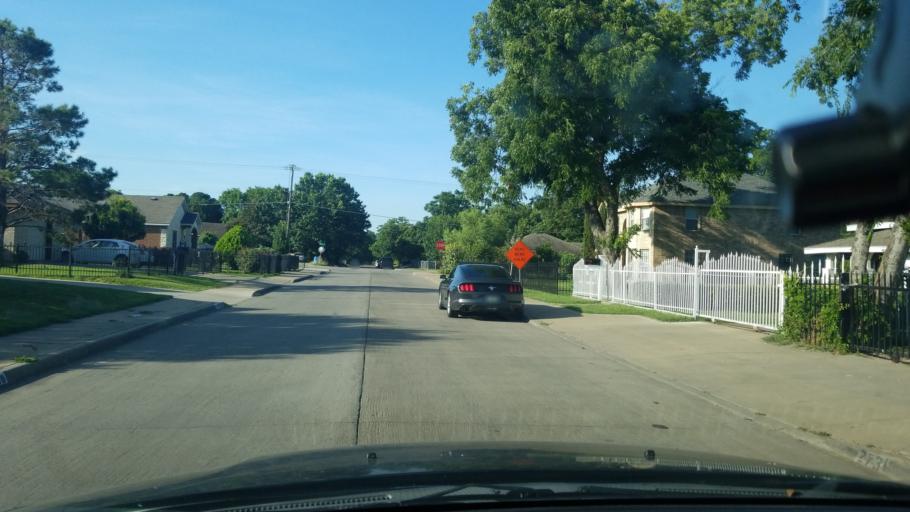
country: US
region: Texas
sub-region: Dallas County
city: Dallas
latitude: 32.7139
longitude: -96.8159
